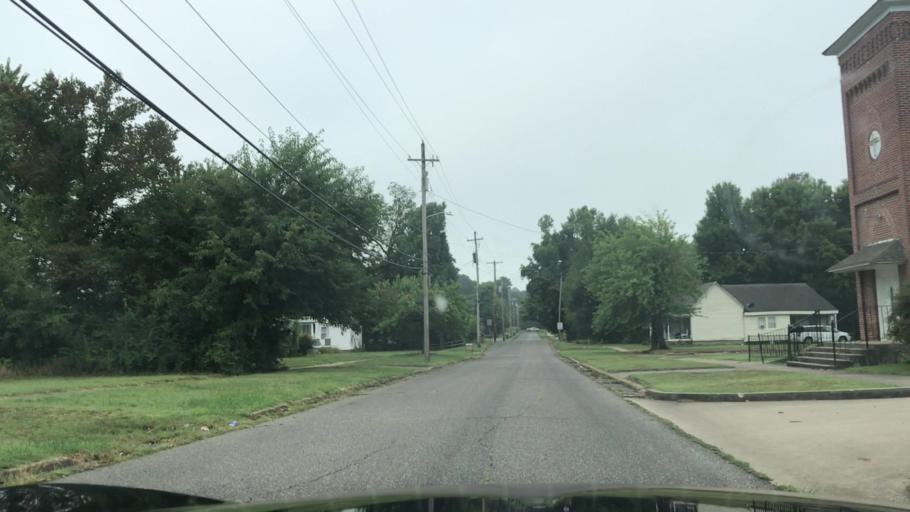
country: US
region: Kentucky
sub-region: Graves County
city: Mayfield
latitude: 36.7379
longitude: -88.6372
